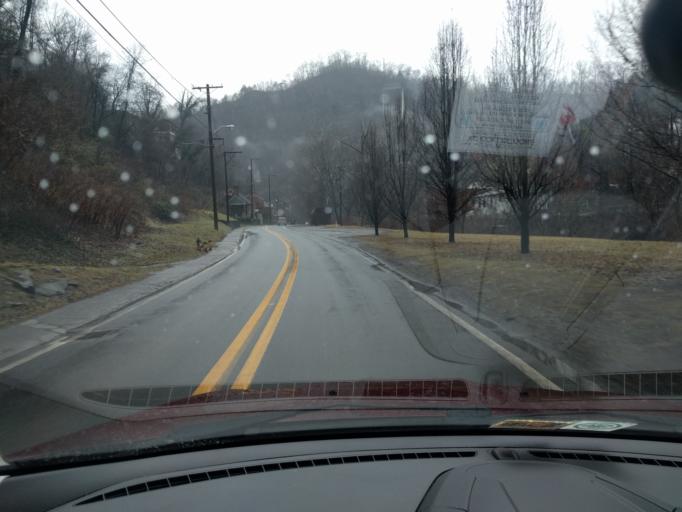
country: US
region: West Virginia
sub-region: McDowell County
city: Welch
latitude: 37.4349
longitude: -81.5774
